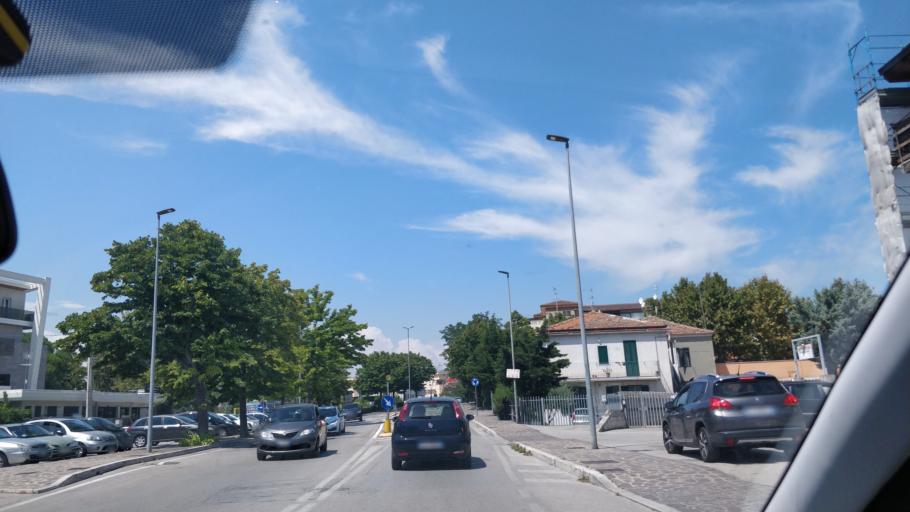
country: IT
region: Abruzzo
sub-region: Provincia di Chieti
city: Francavilla al Mare
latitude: 42.4233
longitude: 14.2809
